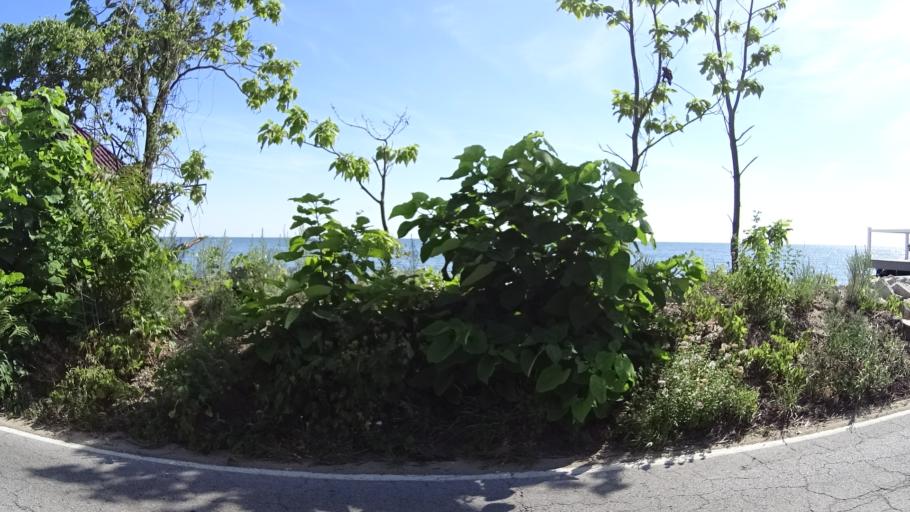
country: US
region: Ohio
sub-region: Erie County
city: Sandusky
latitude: 41.4722
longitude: -82.6703
